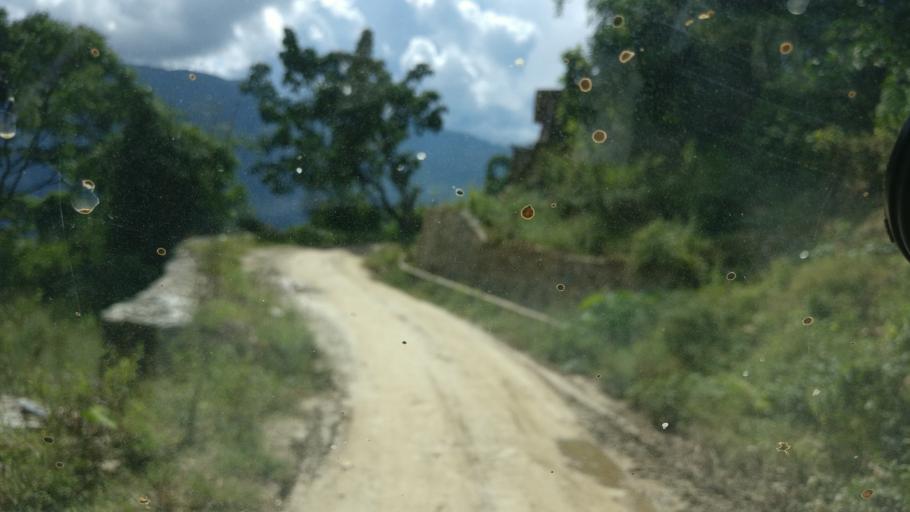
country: NP
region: Western Region
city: Baglung
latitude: 28.2604
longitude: 83.6486
